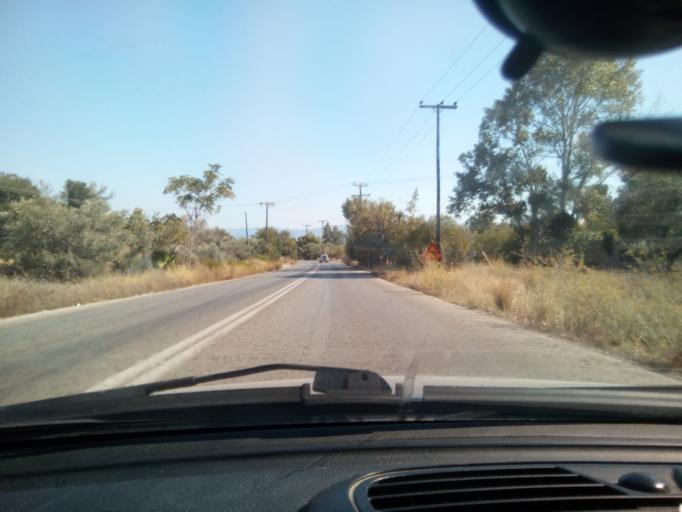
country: GR
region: Central Greece
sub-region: Nomos Evvoias
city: Filla
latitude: 38.4141
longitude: 23.7131
